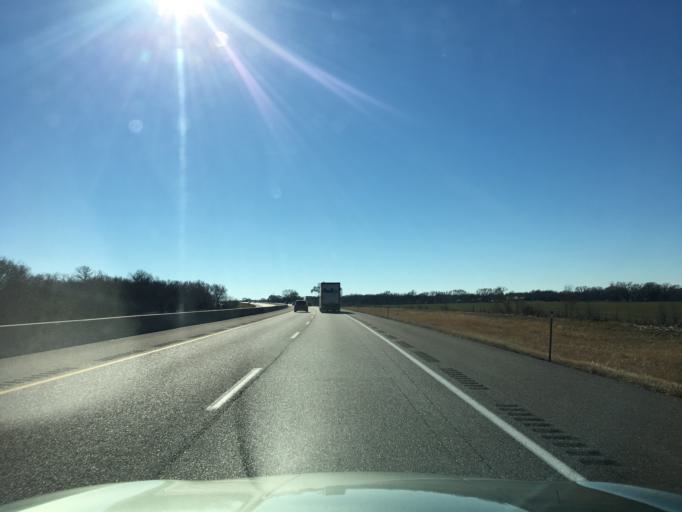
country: US
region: Kansas
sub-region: Sumner County
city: Belle Plaine
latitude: 37.3988
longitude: -97.3259
